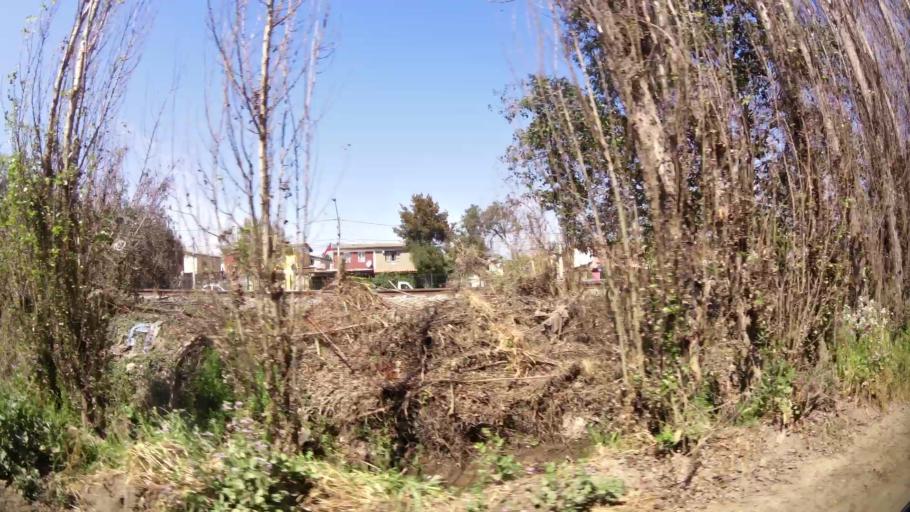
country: CL
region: Santiago Metropolitan
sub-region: Provincia de Talagante
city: Talagante
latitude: -33.6505
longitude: -70.9042
